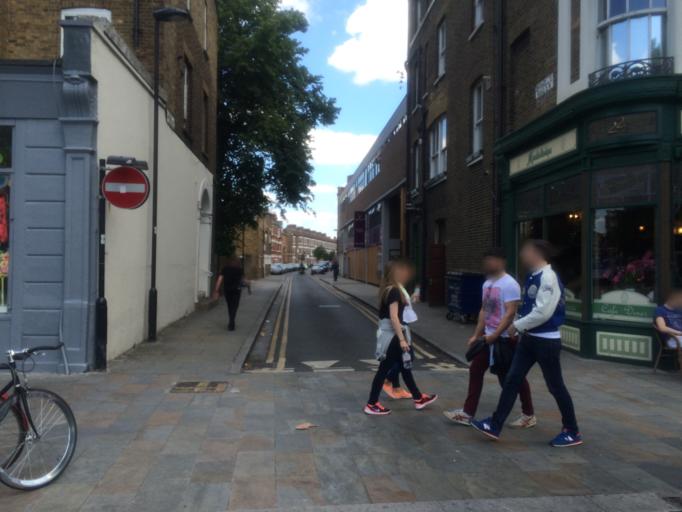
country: GB
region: England
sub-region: Greater London
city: Battersea
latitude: 51.4622
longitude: -0.1402
